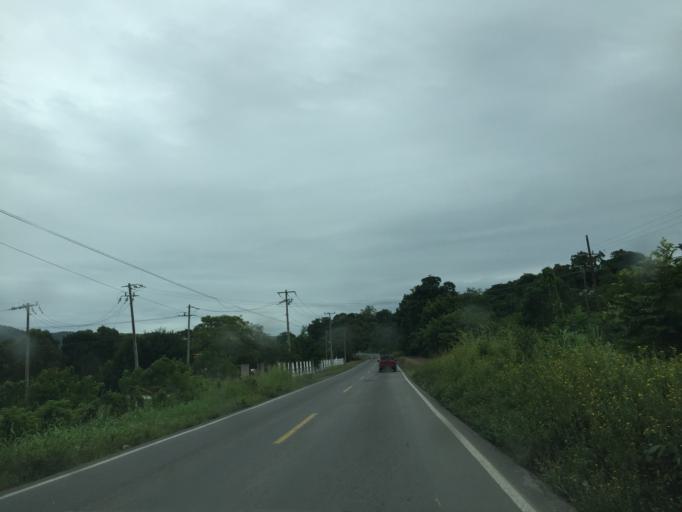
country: MX
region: Veracruz
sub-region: Papantla
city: El Chote
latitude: 20.4386
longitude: -97.3932
